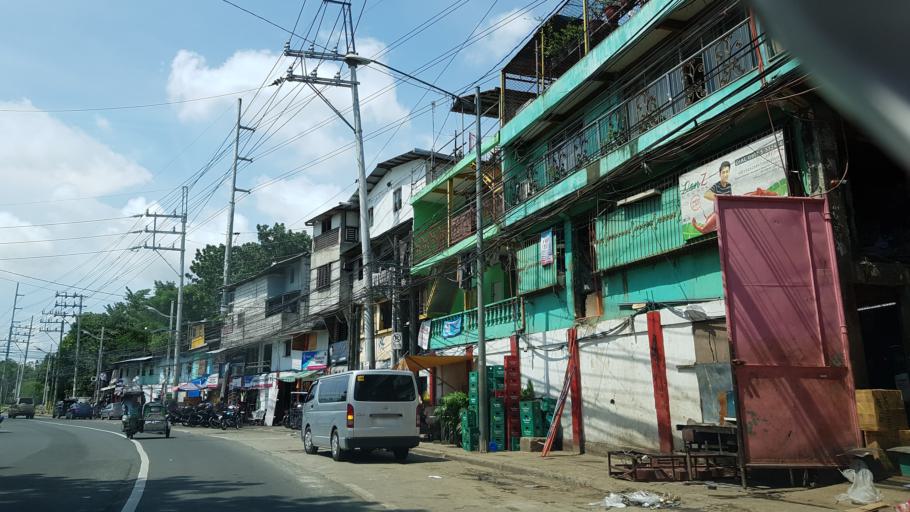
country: PH
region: Metro Manila
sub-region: Makati City
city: Makati City
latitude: 14.5286
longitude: 121.0266
